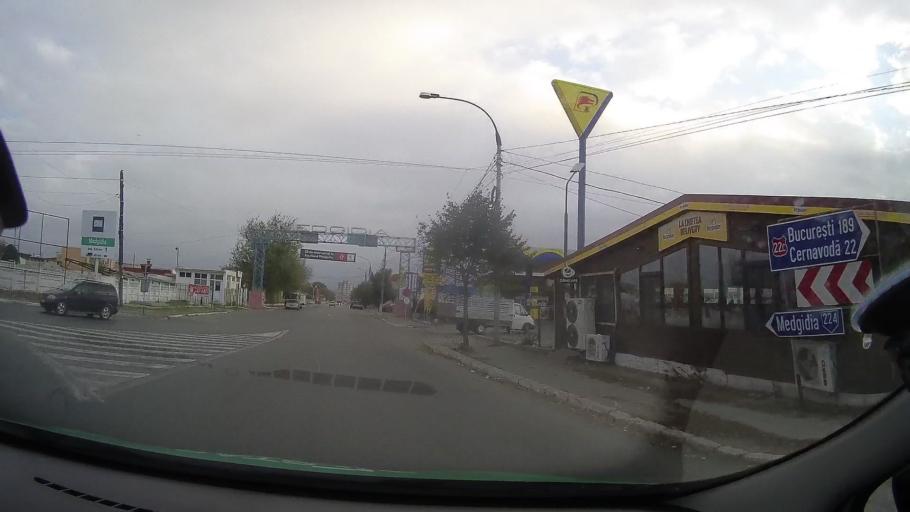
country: RO
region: Constanta
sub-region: Municipiul Medgidia
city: Medgidia
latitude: 44.2664
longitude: 28.2578
